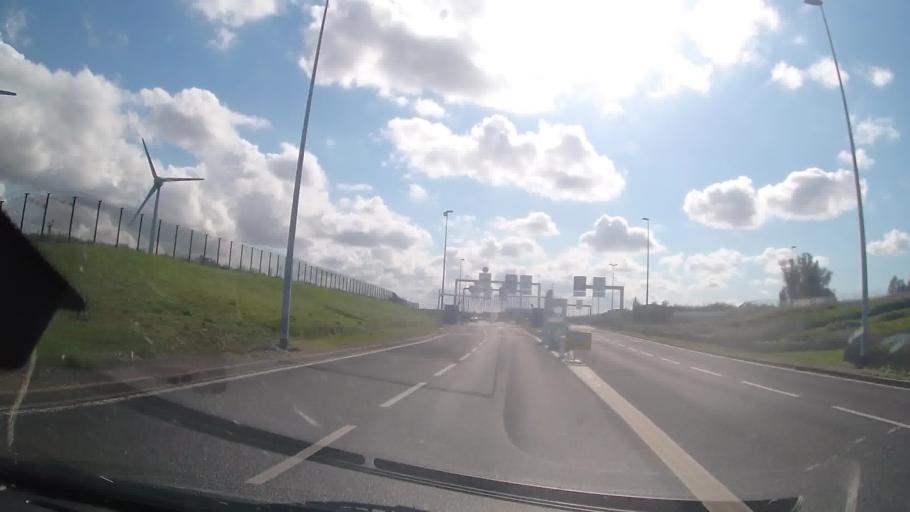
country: FR
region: Nord-Pas-de-Calais
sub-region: Departement du Pas-de-Calais
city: Coquelles
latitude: 50.9304
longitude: 1.8136
